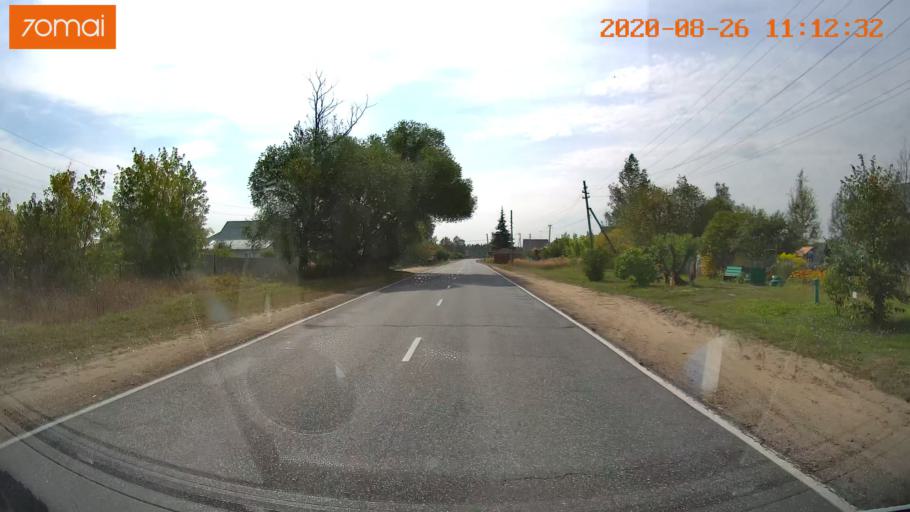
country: RU
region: Rjazan
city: Izhevskoye
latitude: 54.4694
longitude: 41.1250
